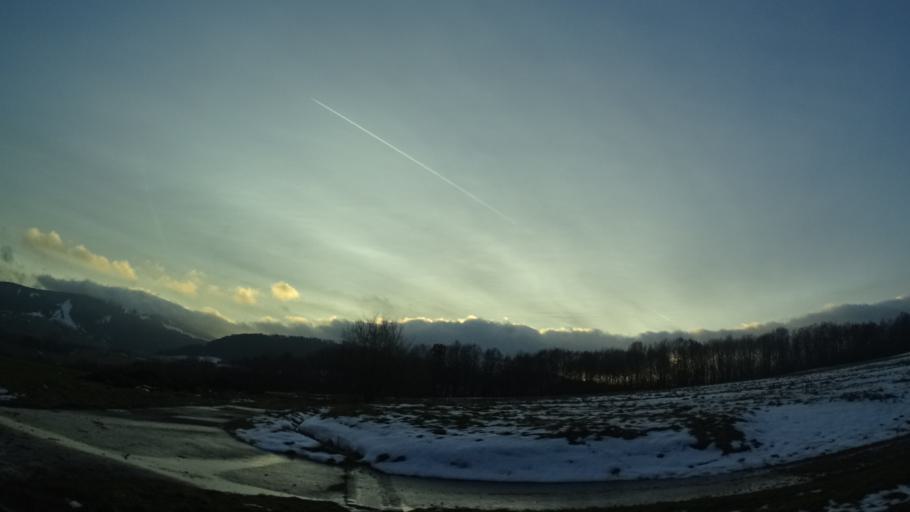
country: DE
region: Bavaria
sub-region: Regierungsbezirk Unterfranken
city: Bischofsheim an der Rhon
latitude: 50.4144
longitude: 10.0010
